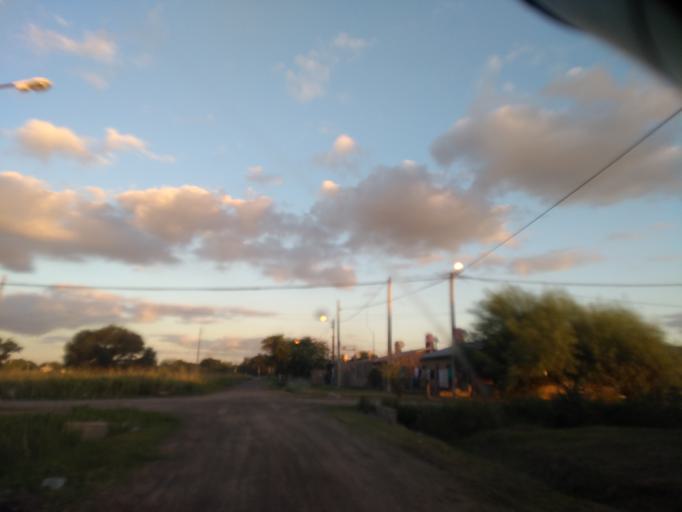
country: AR
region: Chaco
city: Fontana
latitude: -27.4207
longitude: -59.0513
